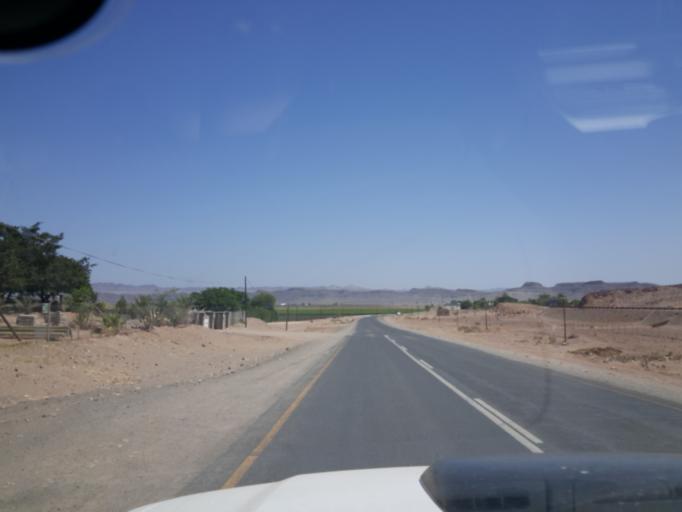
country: ZA
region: Northern Cape
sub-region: Namakwa District Municipality
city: Port Nolloth
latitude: -28.7346
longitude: 17.6161
